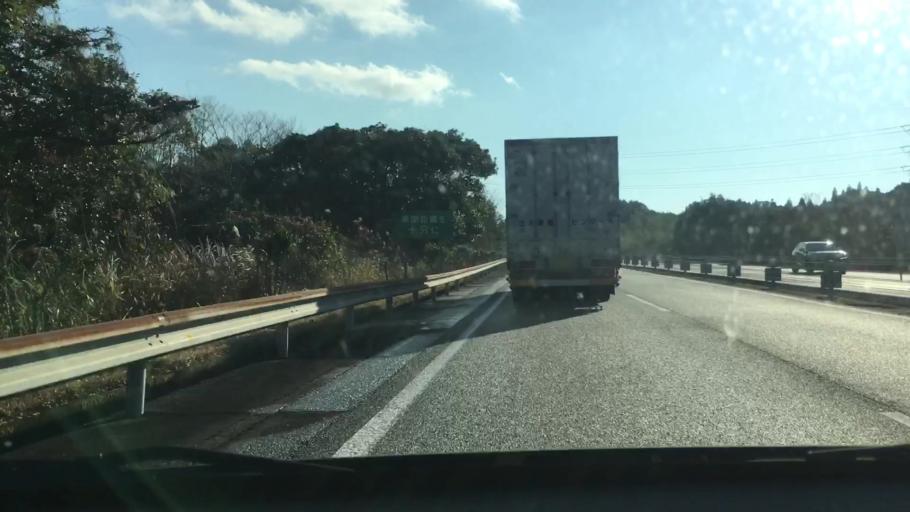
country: JP
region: Kagoshima
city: Okuchi-shinohara
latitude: 31.9331
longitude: 130.7066
